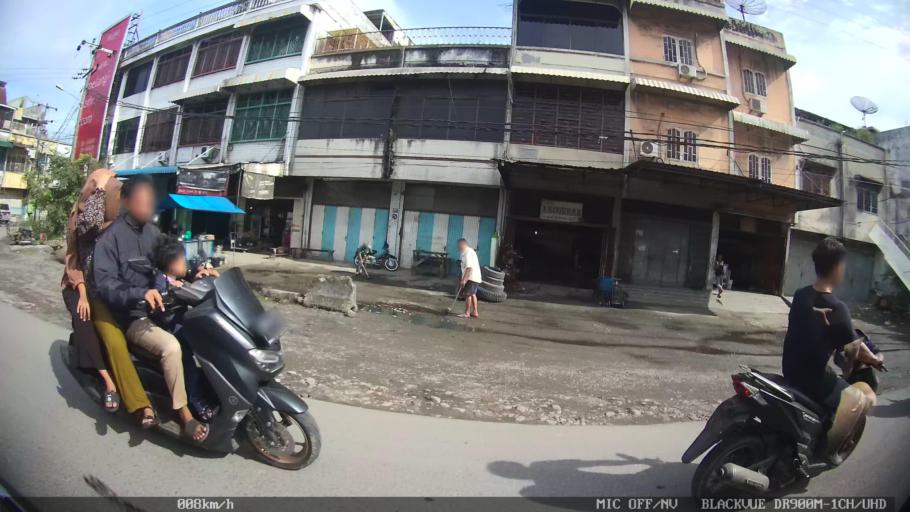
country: ID
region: North Sumatra
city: Medan
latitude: 3.6271
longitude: 98.6605
